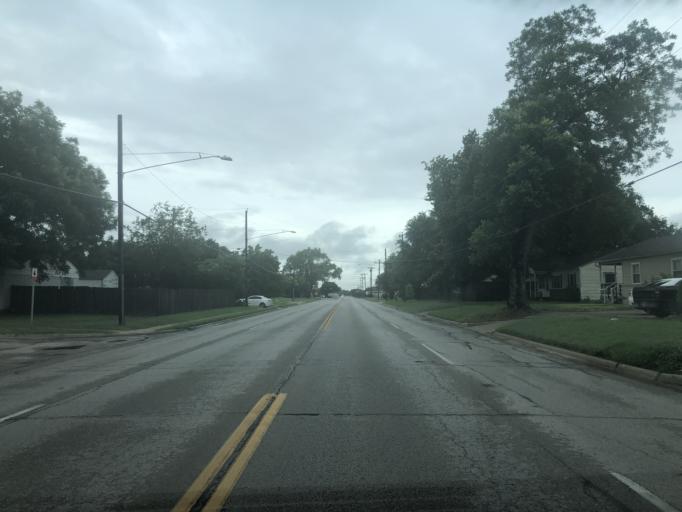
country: US
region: Texas
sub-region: Dallas County
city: Irving
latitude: 32.8012
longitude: -96.9506
